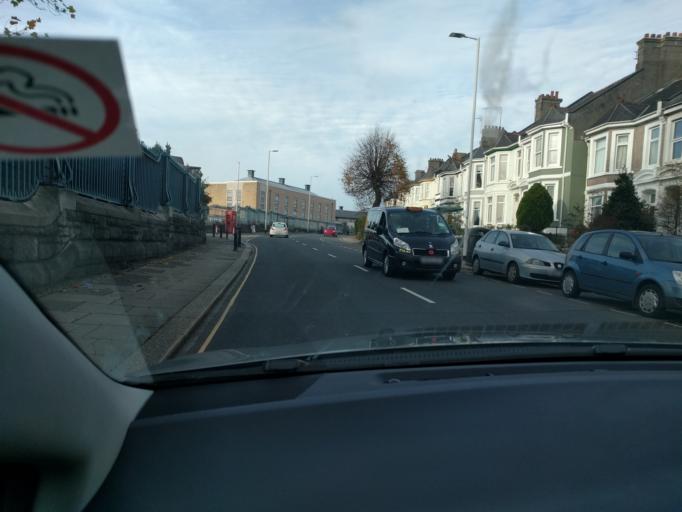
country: GB
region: England
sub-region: Cornwall
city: Torpoint
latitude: 50.3901
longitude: -4.1807
